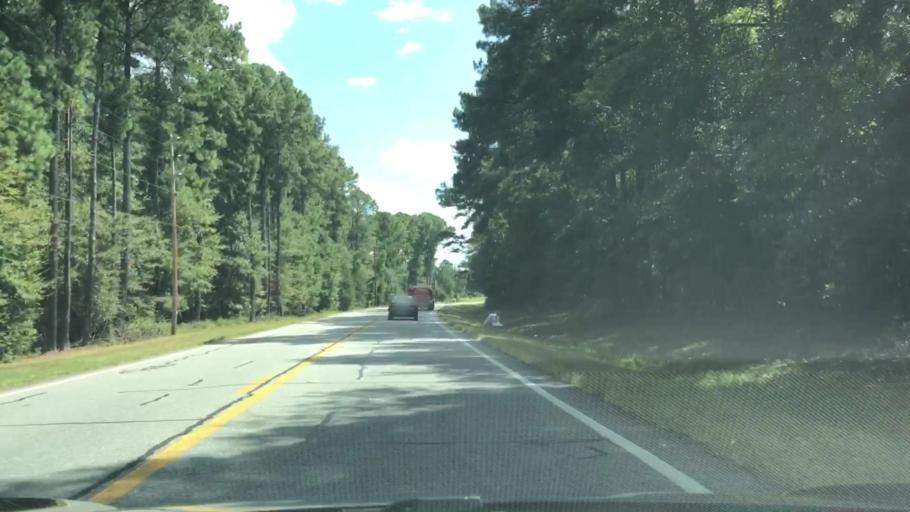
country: US
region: Georgia
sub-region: Oconee County
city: Watkinsville
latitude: 33.7834
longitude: -83.3138
